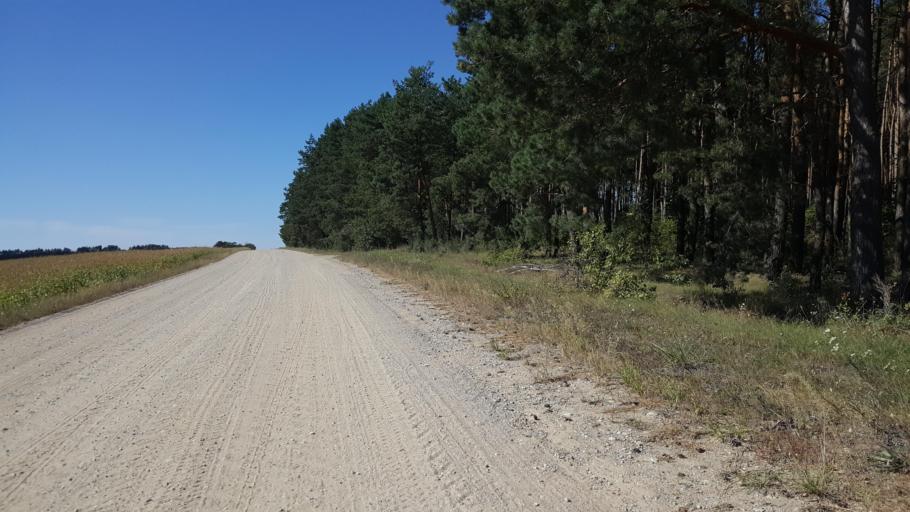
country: PL
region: Lublin Voivodeship
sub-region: Powiat bialski
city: Rokitno
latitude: 52.2261
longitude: 23.3359
